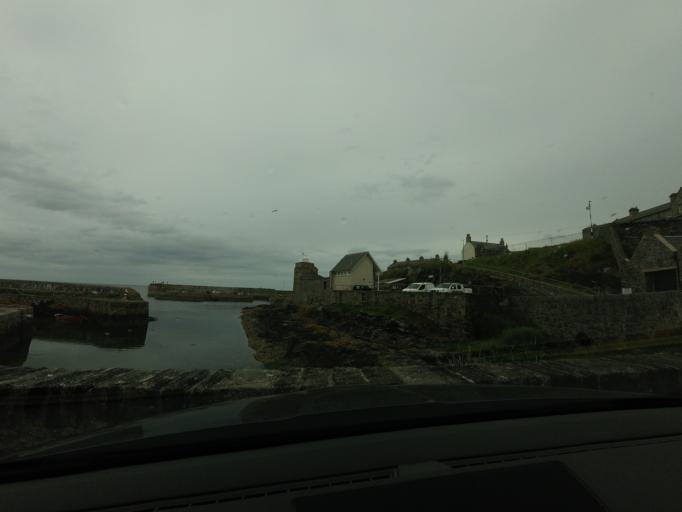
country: GB
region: Scotland
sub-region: Aberdeenshire
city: Portsoy
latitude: 57.6845
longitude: -2.6907
